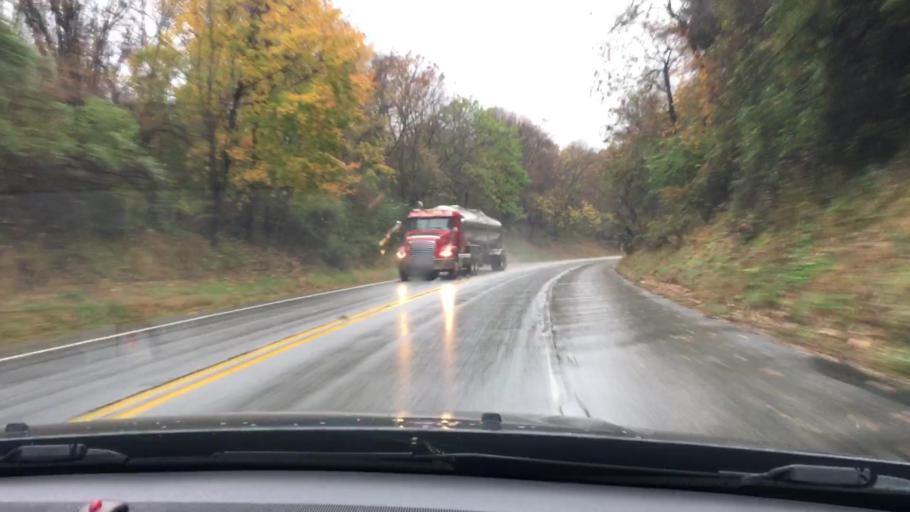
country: US
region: Pennsylvania
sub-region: York County
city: Susquehanna Trails
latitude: 39.8282
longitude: -76.3104
